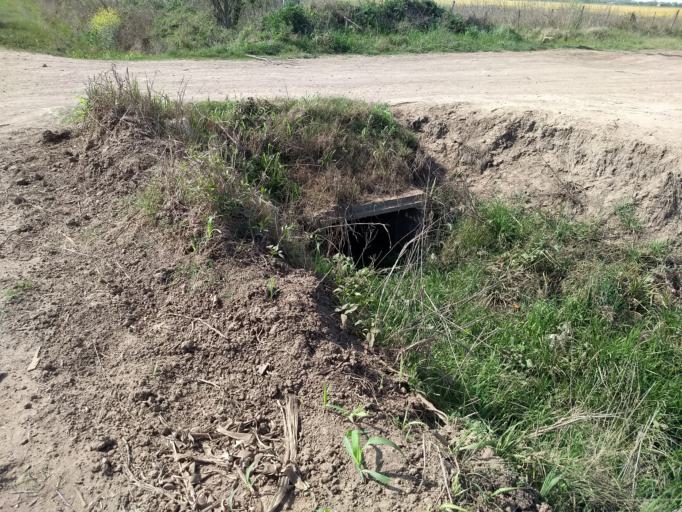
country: AR
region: Santa Fe
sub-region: Departamento de San Lorenzo
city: San Lorenzo
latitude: -32.6563
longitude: -60.8071
